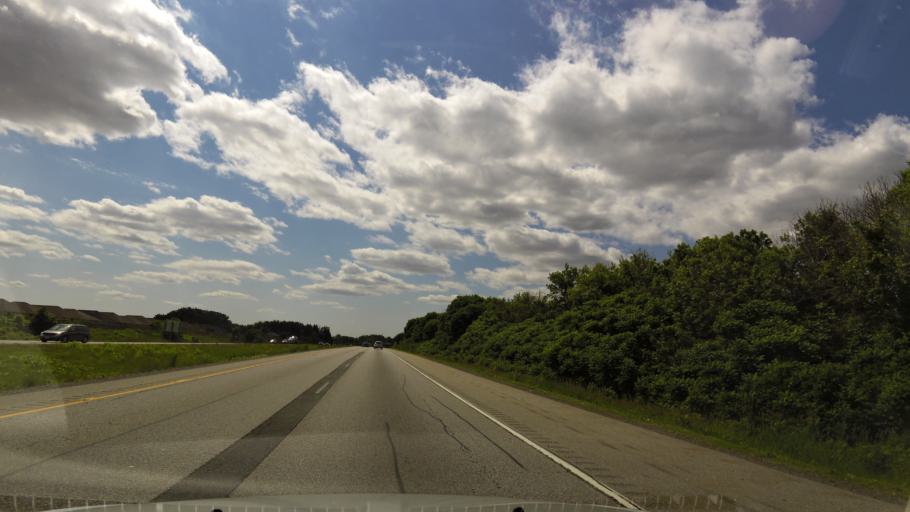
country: CA
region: Ontario
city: Ancaster
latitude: 43.2046
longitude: -79.9920
